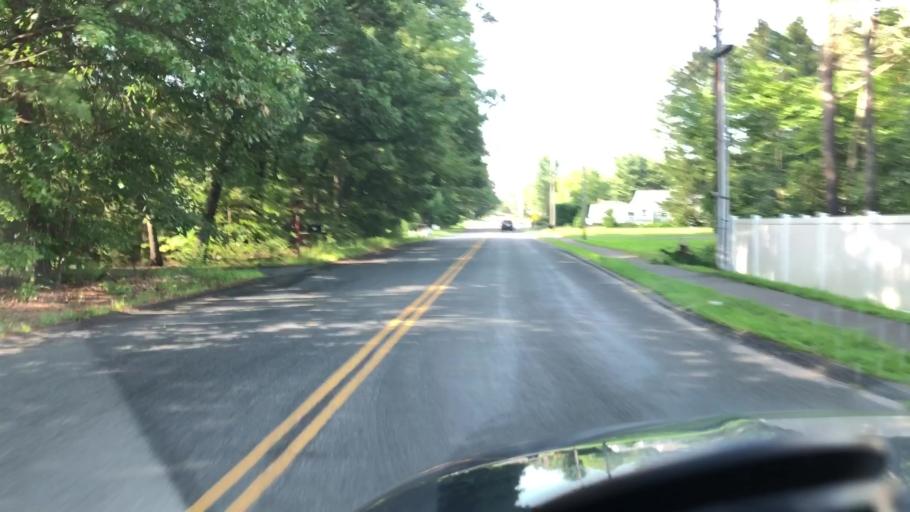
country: US
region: Massachusetts
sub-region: Hampshire County
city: Southampton
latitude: 42.2262
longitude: -72.6866
